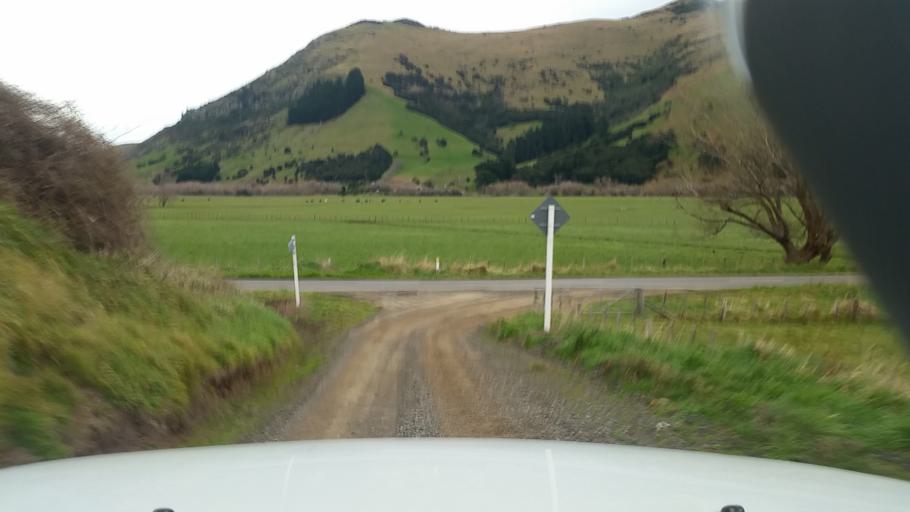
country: NZ
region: Canterbury
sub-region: Christchurch City
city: Christchurch
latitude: -43.7784
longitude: 172.7917
